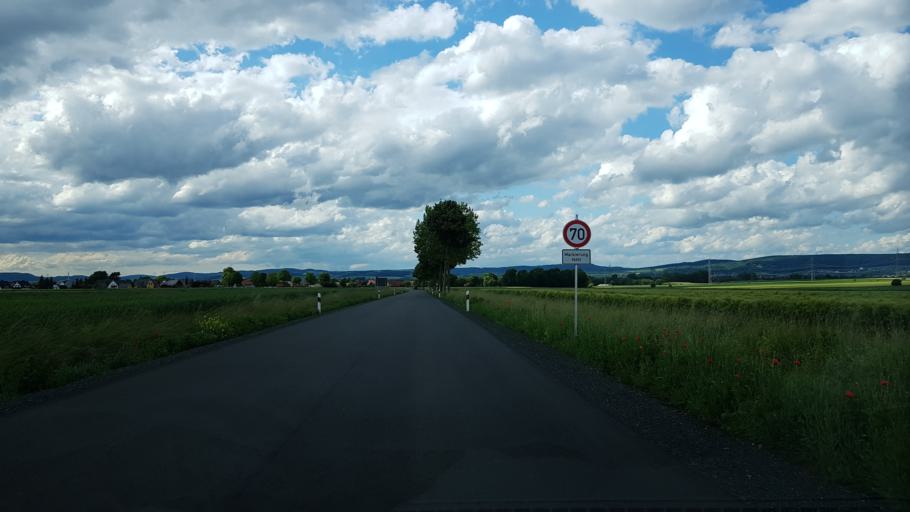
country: DE
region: Lower Saxony
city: Einbeck
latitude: 51.7605
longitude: 9.8711
